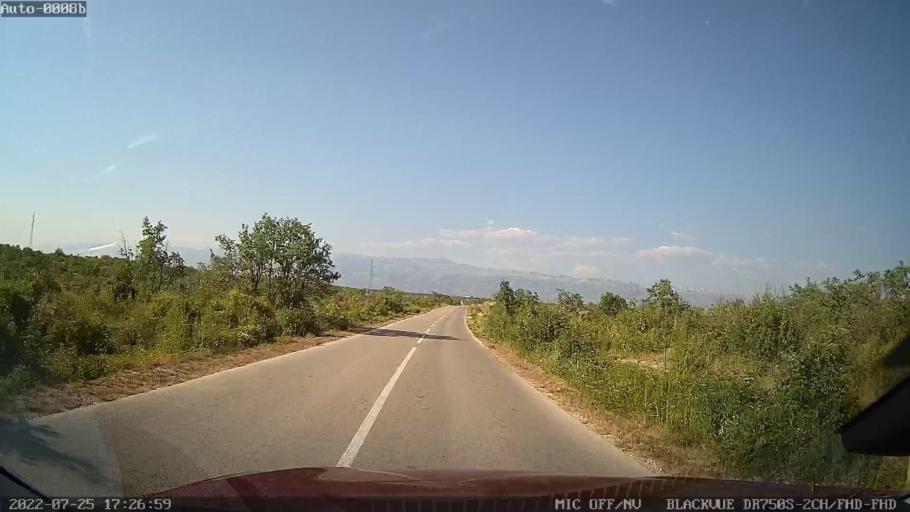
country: HR
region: Zadarska
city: Pridraga
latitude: 44.1388
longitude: 15.5029
